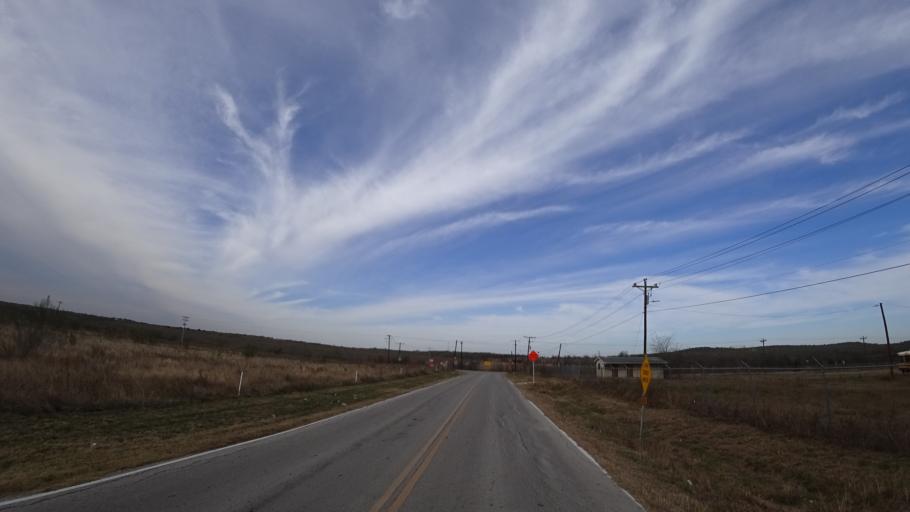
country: US
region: Texas
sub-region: Travis County
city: Onion Creek
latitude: 30.1451
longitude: -97.6987
